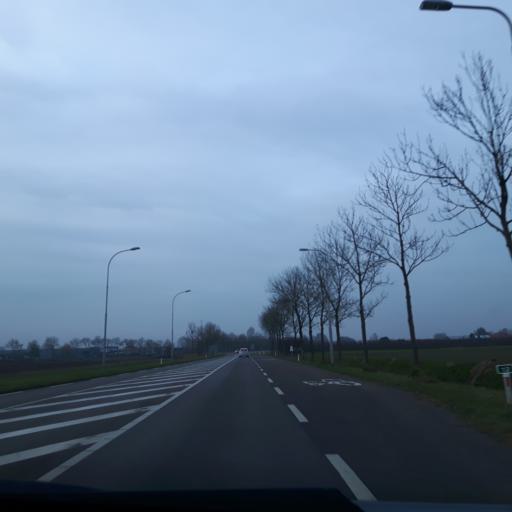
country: NL
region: Zeeland
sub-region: Gemeente Goes
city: Goes
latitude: 51.4549
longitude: 3.8868
